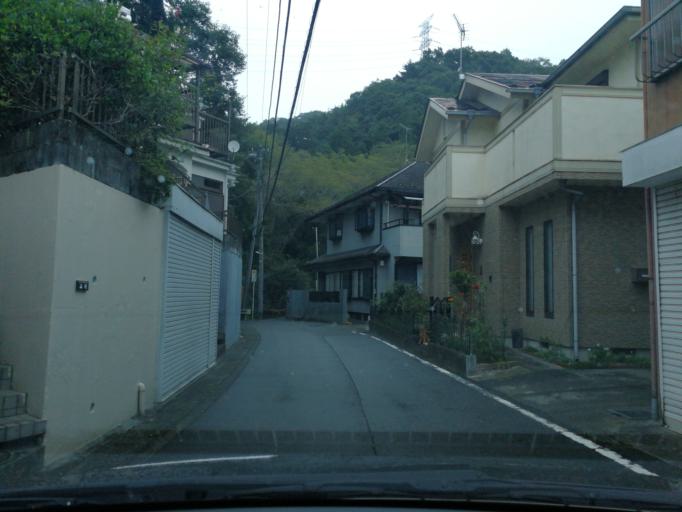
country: JP
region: Yamanashi
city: Uenohara
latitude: 35.6120
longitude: 139.2204
